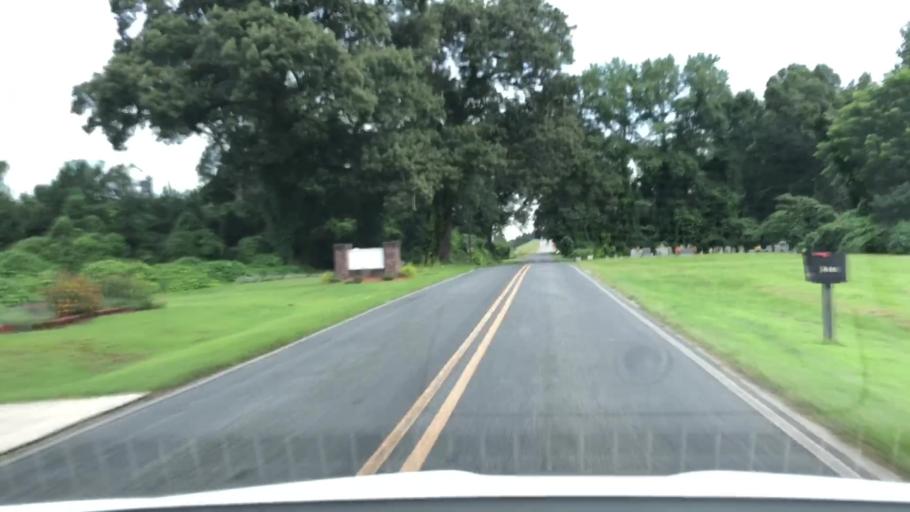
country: US
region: North Carolina
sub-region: Jones County
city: Maysville
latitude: 34.9074
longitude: -77.2335
